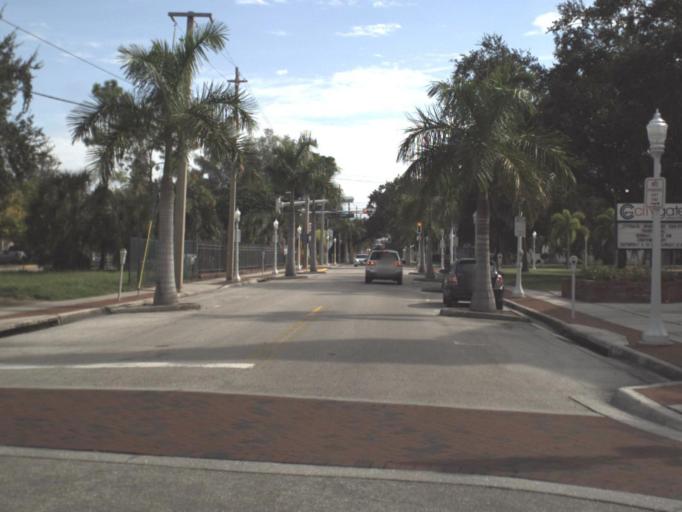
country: US
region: Florida
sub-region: Lee County
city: North Fort Myers
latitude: 26.6430
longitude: -81.8678
